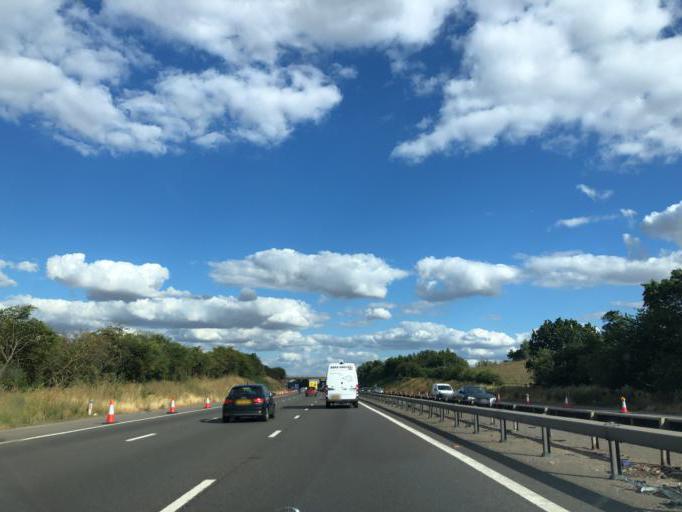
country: GB
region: England
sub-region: Milton Keynes
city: Woburn Sands
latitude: 52.0388
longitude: -0.6472
